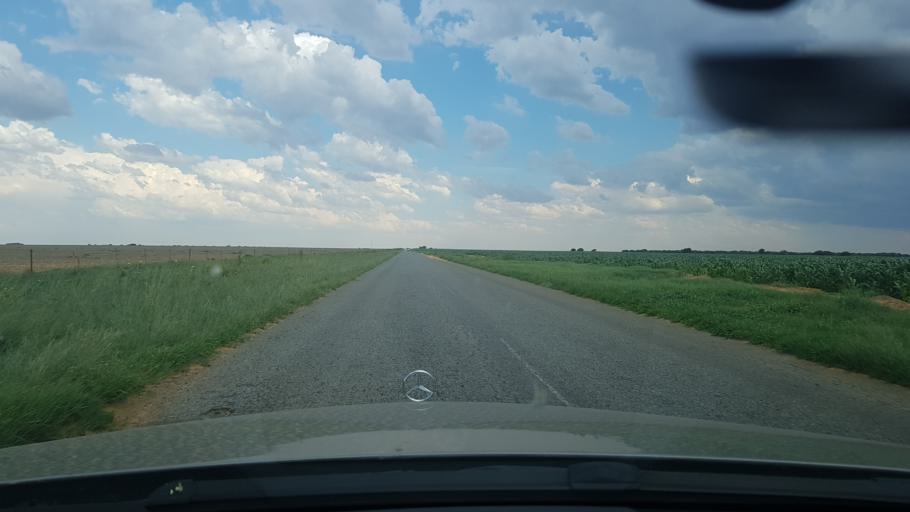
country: ZA
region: Orange Free State
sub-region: Lejweleputswa District Municipality
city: Hoopstad
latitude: -27.8971
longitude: 25.6729
